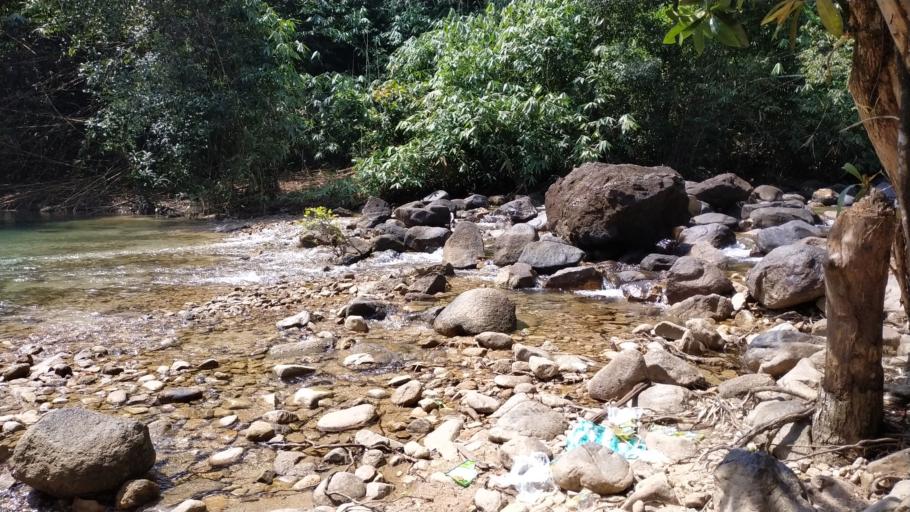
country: MM
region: Tanintharyi
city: Dawei
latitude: 14.5842
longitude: 98.0501
